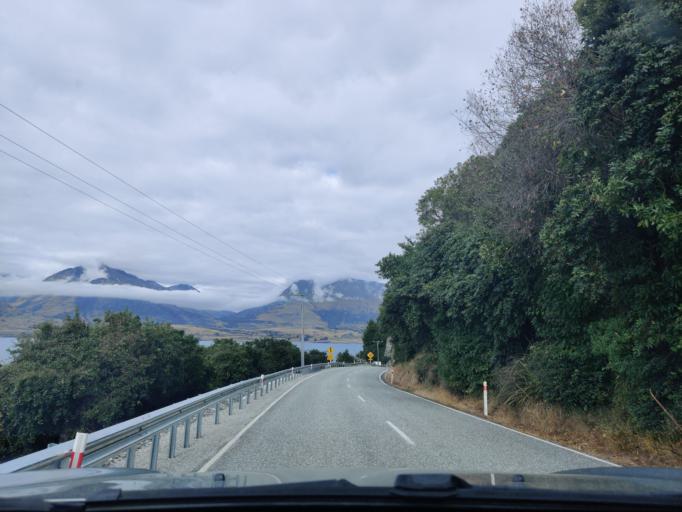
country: NZ
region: Otago
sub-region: Queenstown-Lakes District
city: Queenstown
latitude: -45.0765
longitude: 168.4904
